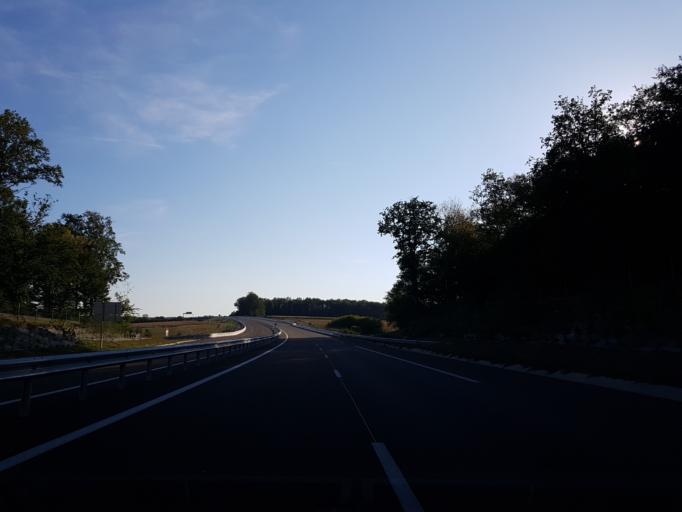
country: FR
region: Franche-Comte
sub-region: Departement de la Haute-Saone
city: Magny-Vernois
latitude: 47.6896
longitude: 6.4431
